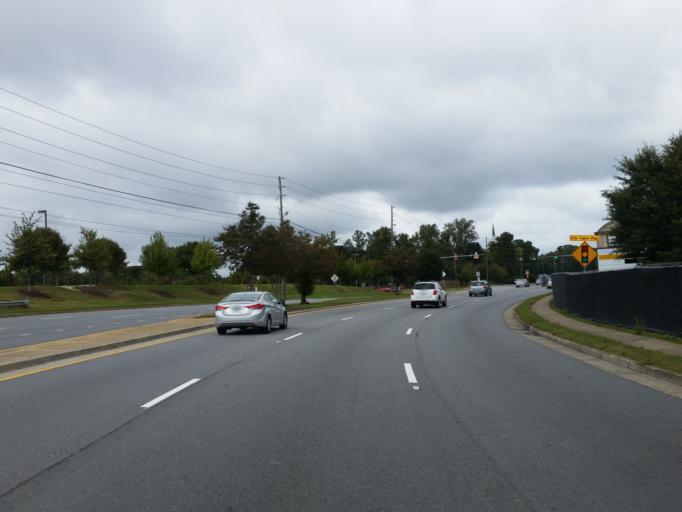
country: US
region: Georgia
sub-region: Fulton County
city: Sandy Springs
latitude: 33.9681
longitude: -84.4135
